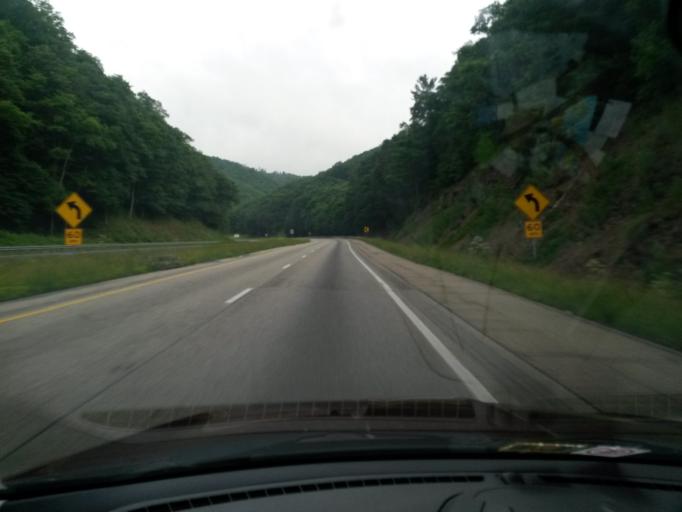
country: US
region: West Virginia
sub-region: Greenbrier County
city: White Sulphur Springs
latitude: 37.8226
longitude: -80.1620
